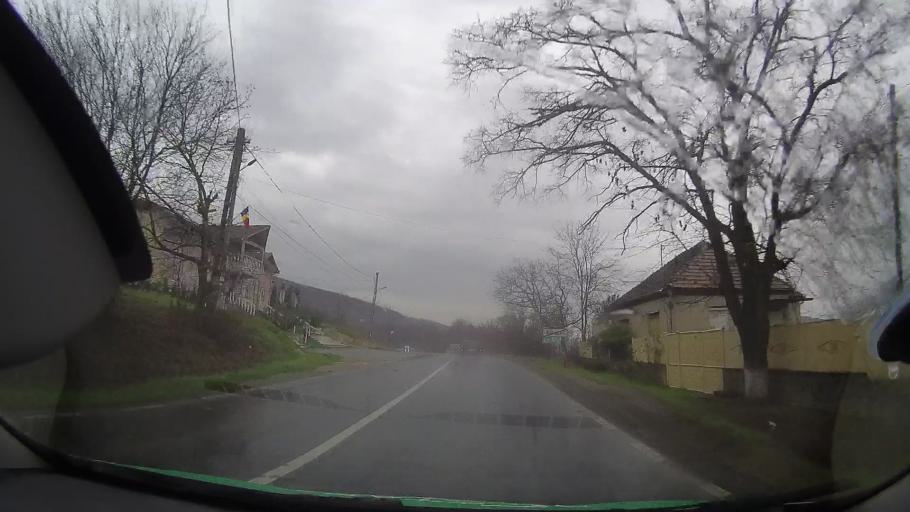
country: RO
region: Bihor
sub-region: Comuna Rabagani
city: Rabagani
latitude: 46.7513
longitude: 22.2126
